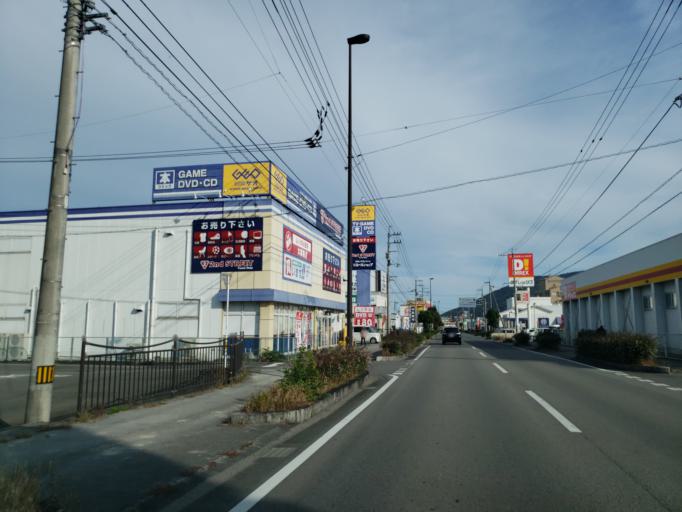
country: JP
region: Tokushima
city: Wakimachi
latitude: 34.0646
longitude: 134.1536
